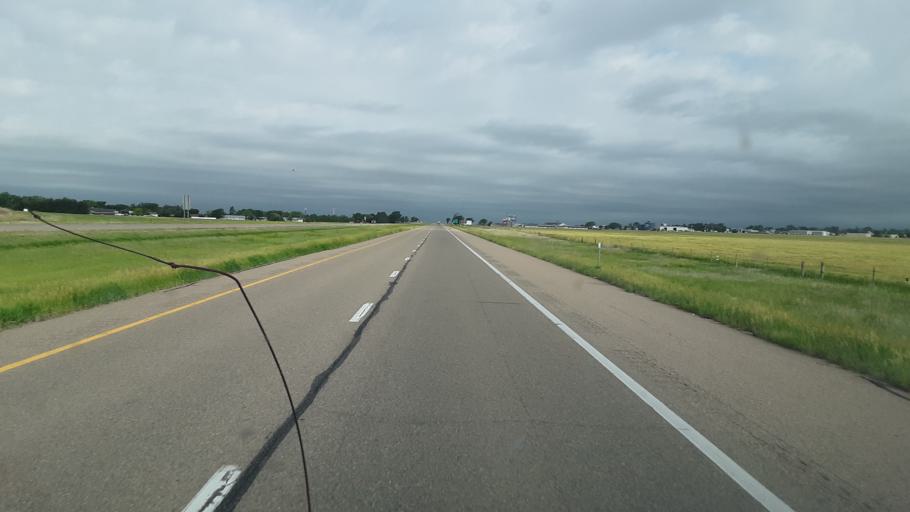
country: US
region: Kansas
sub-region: Gove County
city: Gove
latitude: 39.0528
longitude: -100.2304
